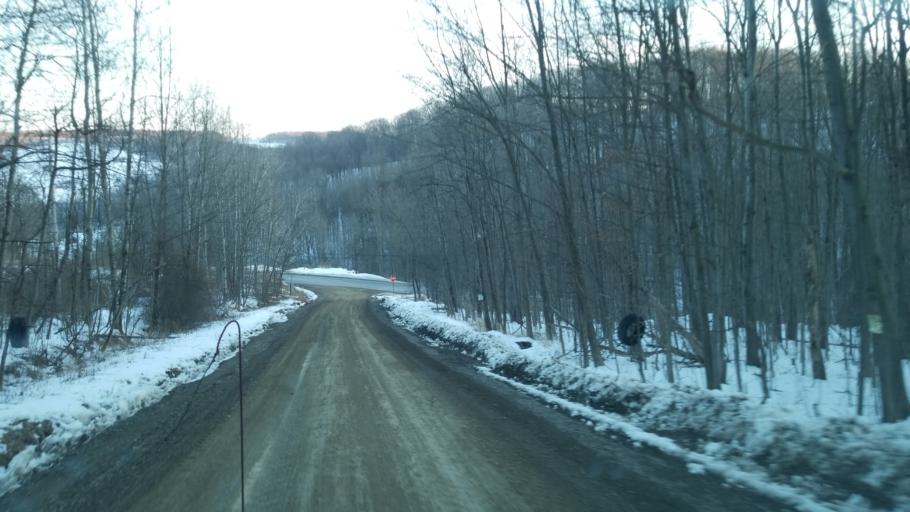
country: US
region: Pennsylvania
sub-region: Tioga County
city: Westfield
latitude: 42.0241
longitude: -77.6194
